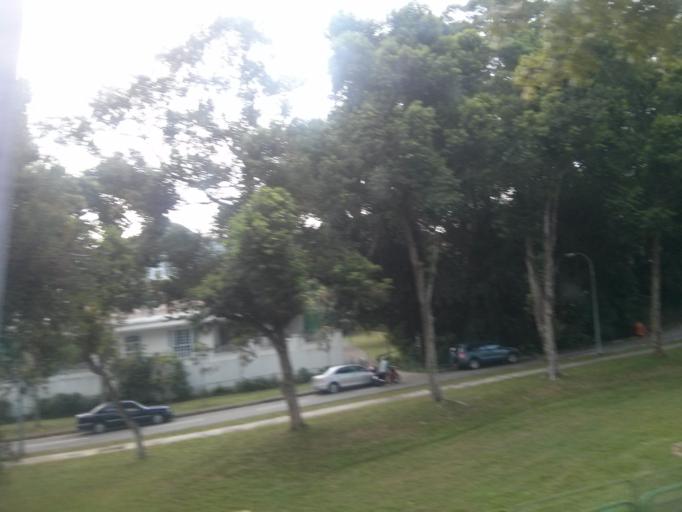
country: SG
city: Singapore
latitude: 1.3456
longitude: 103.8382
